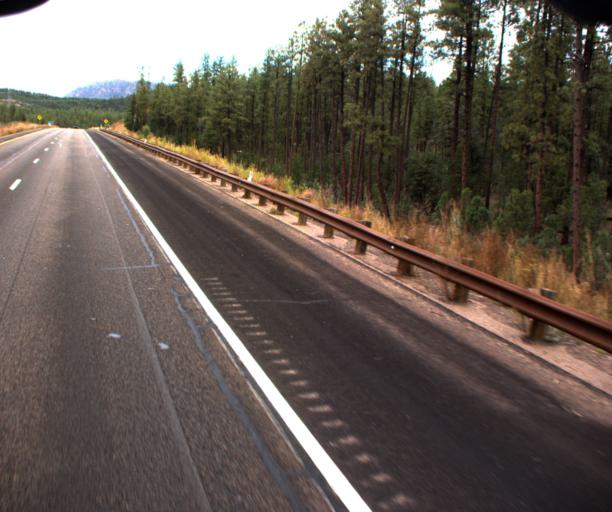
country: US
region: Arizona
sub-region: Gila County
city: Star Valley
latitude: 34.3131
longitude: -111.1118
